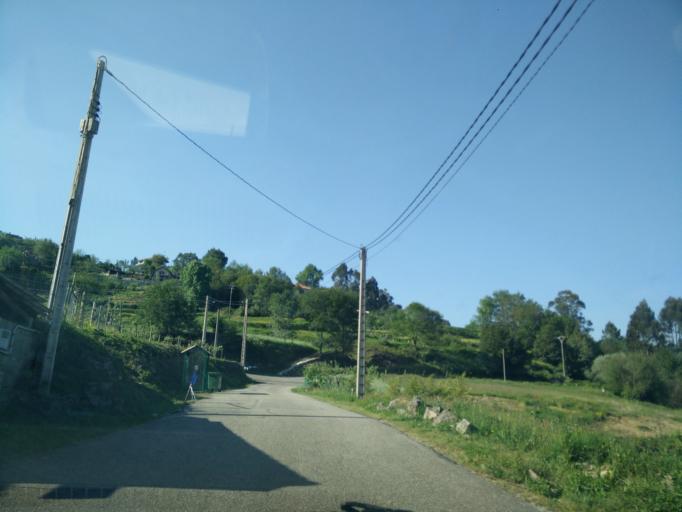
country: ES
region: Galicia
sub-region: Provincia de Pontevedra
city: Mondariz
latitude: 42.2527
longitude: -8.4241
